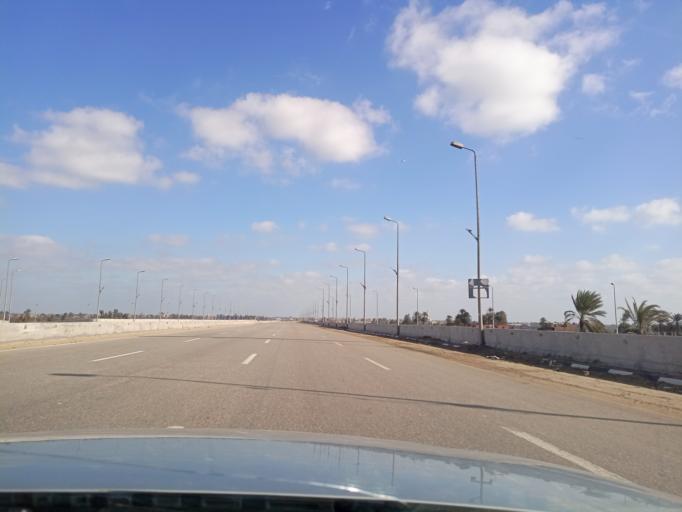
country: EG
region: Muhafazat al Minufiyah
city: Ashmun
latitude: 30.3232
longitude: 30.8309
